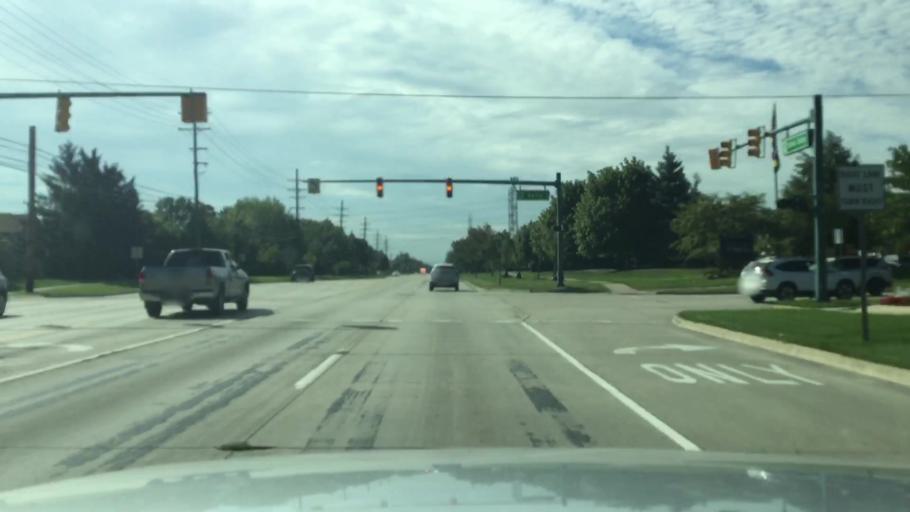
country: US
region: Michigan
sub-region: Wayne County
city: Canton
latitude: 42.3150
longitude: -83.4877
